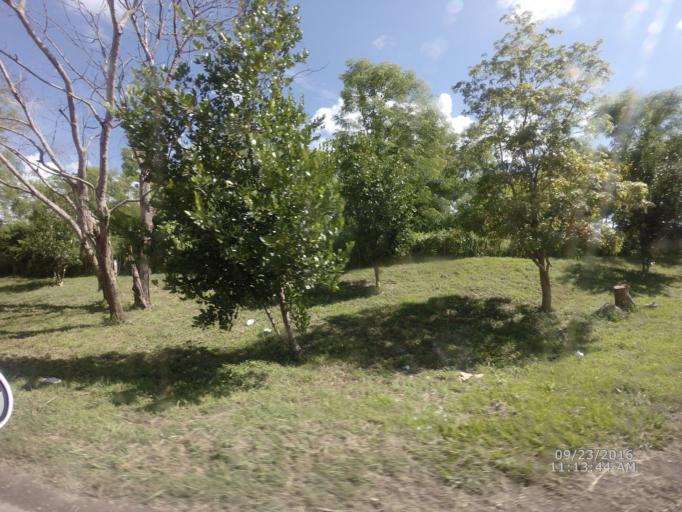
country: CU
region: La Habana
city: Arroyo Naranjo
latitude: 23.0314
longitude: -82.2997
